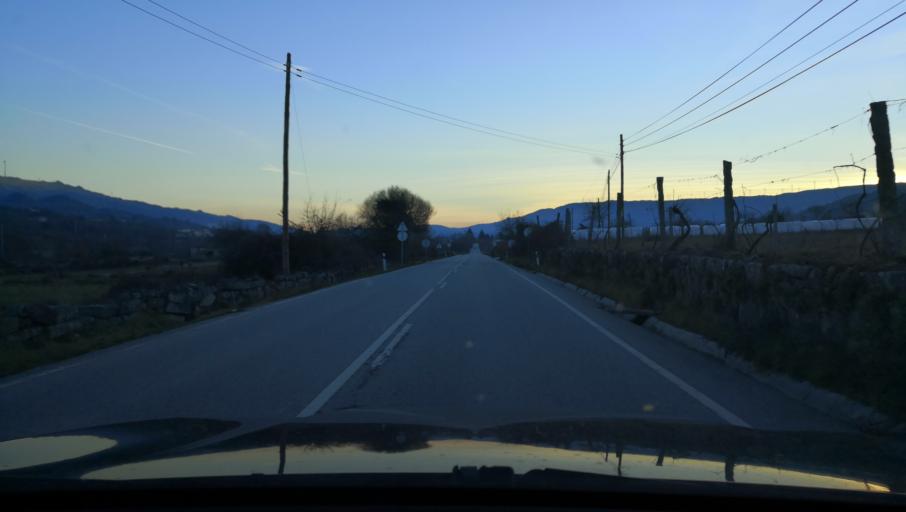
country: PT
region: Vila Real
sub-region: Vila Pouca de Aguiar
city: Vila Pouca de Aguiar
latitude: 41.4799
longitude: -7.6556
